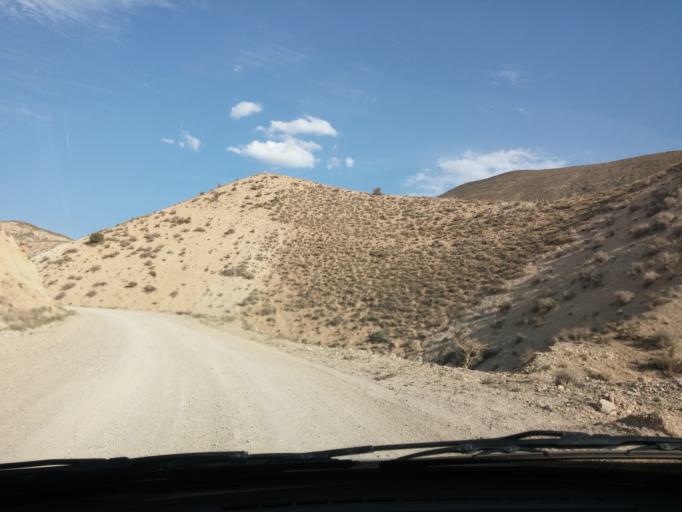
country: IR
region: Tehran
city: Damavand
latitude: 35.5355
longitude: 52.1969
